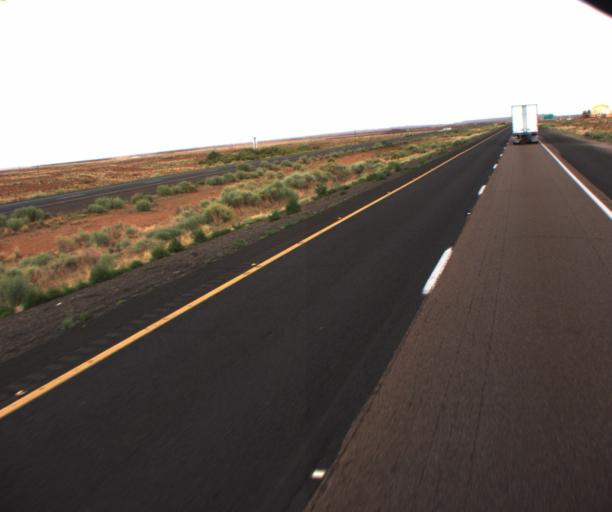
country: US
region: Arizona
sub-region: Coconino County
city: LeChee
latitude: 35.0955
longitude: -110.9406
